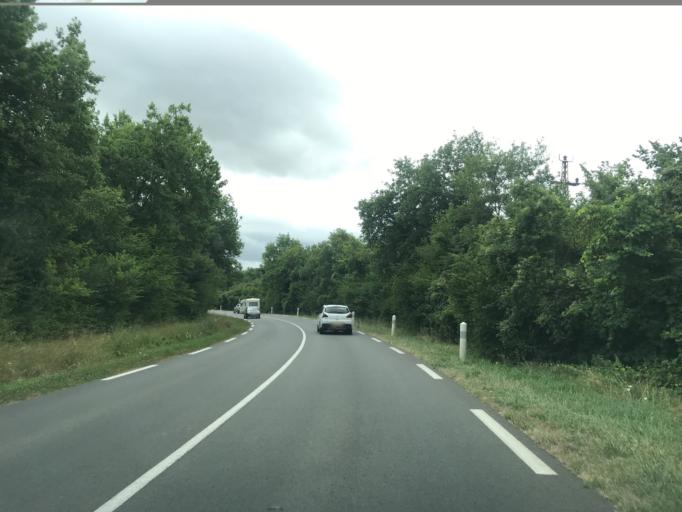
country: FR
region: Aquitaine
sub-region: Departement de la Dordogne
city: Mareuil
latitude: 45.4856
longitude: 0.3660
